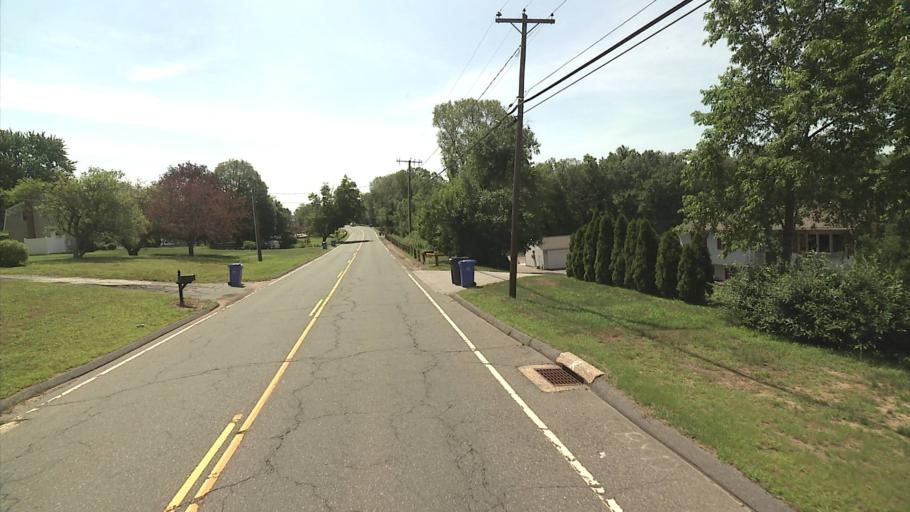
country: US
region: Connecticut
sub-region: Tolland County
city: Mansfield City
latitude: 41.7428
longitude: -72.2618
